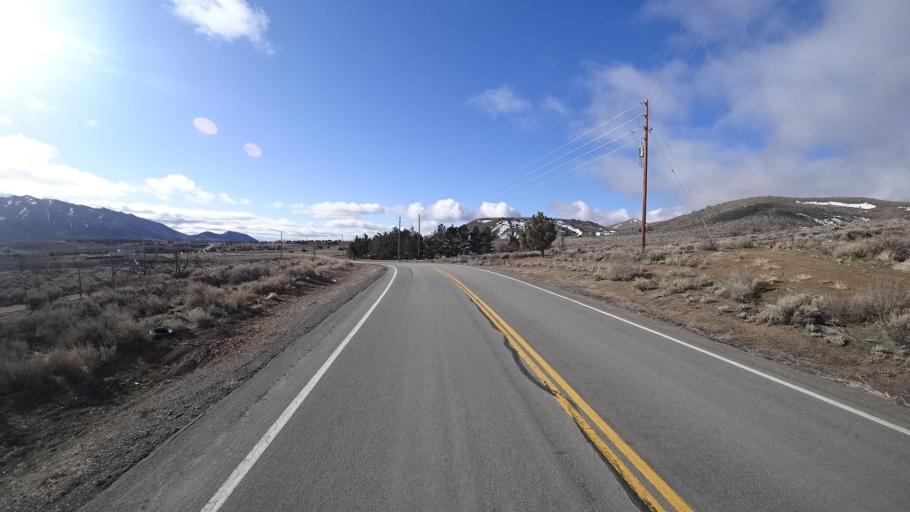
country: US
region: Nevada
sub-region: Washoe County
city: Cold Springs
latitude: 39.7888
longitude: -119.8995
